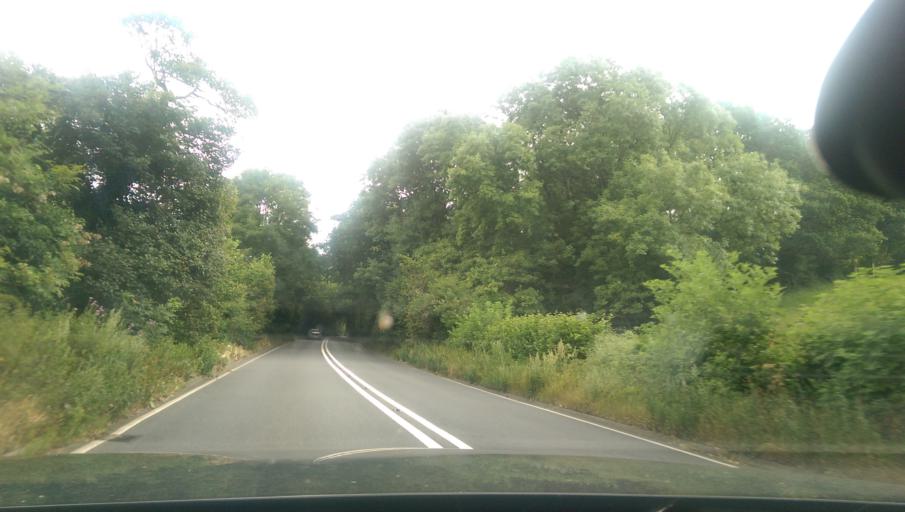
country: GB
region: England
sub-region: Devon
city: Honiton
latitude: 50.8382
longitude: -3.1403
